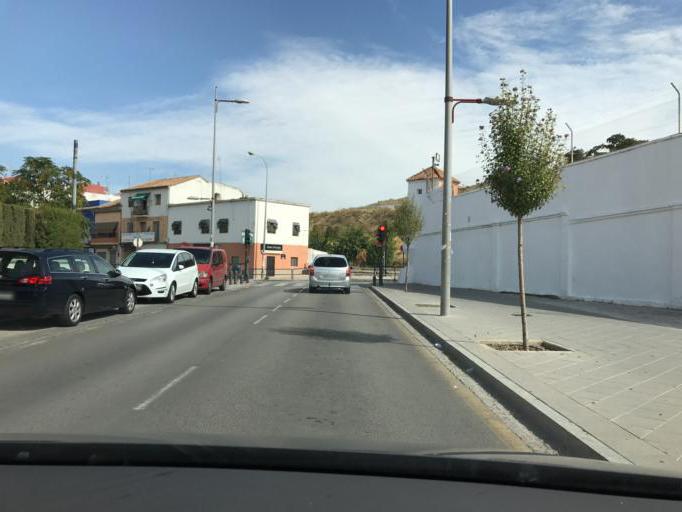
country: ES
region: Andalusia
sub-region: Provincia de Granada
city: Granada
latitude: 37.1953
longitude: -3.6018
